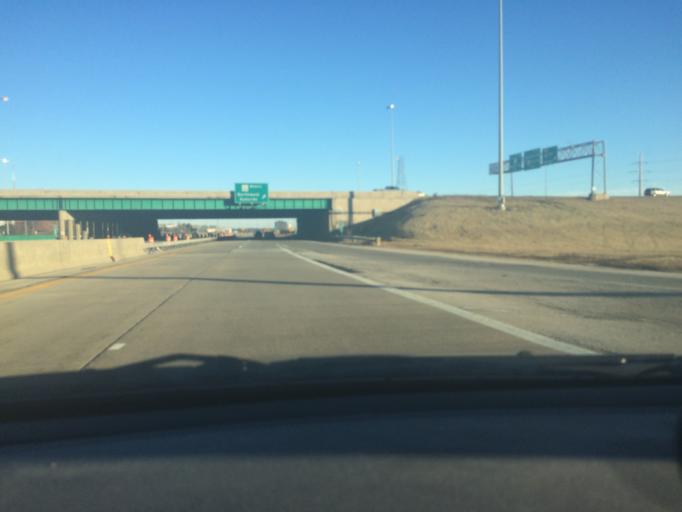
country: US
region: Illinois
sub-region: Cook County
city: Rolling Meadows
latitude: 42.0576
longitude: -88.0301
